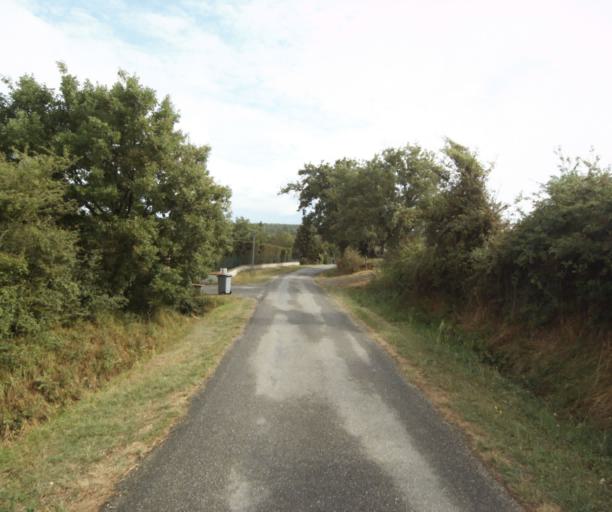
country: FR
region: Midi-Pyrenees
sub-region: Departement de la Haute-Garonne
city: Revel
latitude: 43.4258
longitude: 1.9847
